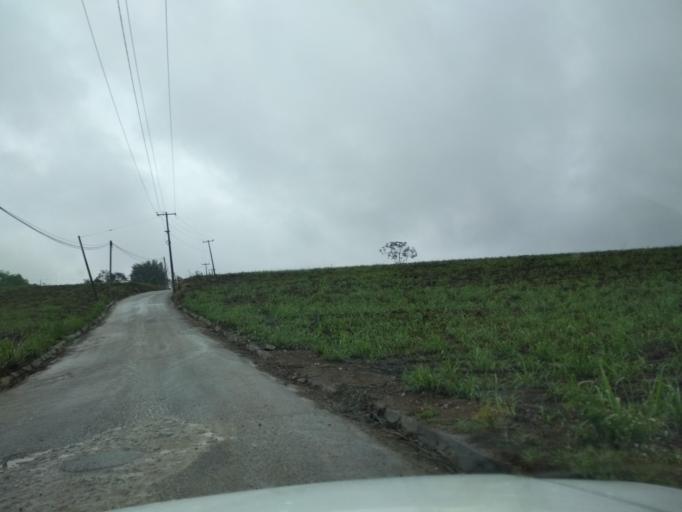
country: MX
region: Veracruz
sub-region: Amatlan de los Reyes
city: Centro de Readaptacion Social
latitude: 18.8302
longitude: -96.9324
